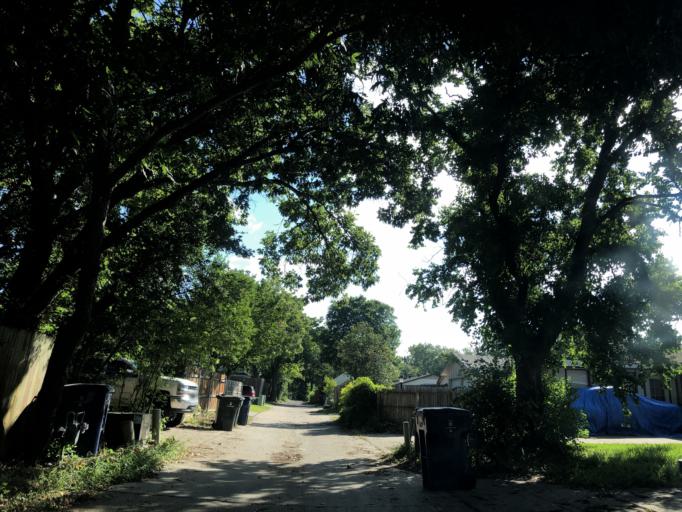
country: US
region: Texas
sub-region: Dallas County
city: Garland
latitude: 32.8568
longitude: -96.6420
